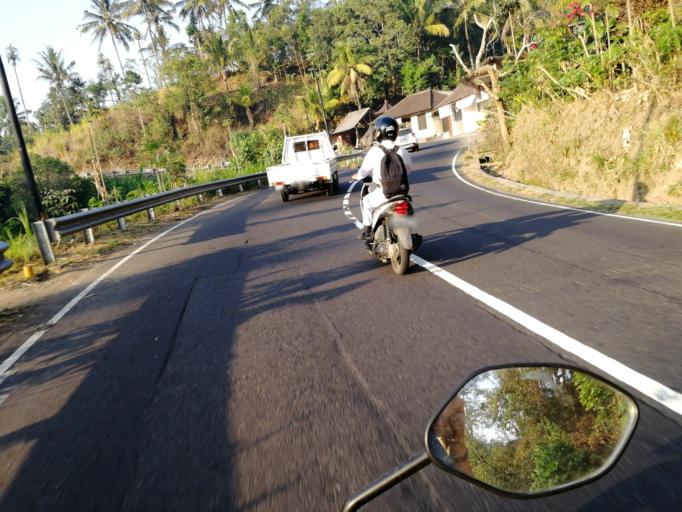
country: ID
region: Bali
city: Tistagede
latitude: -8.3734
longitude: 115.6095
